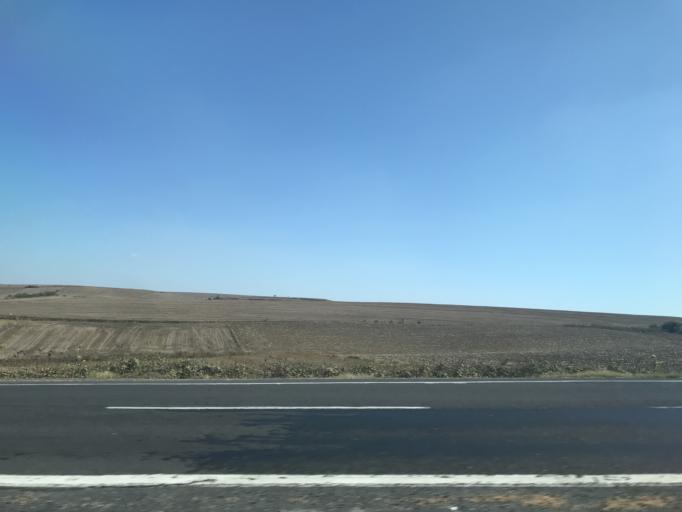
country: TR
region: Tekirdag
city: Muratli
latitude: 41.0968
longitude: 27.4939
